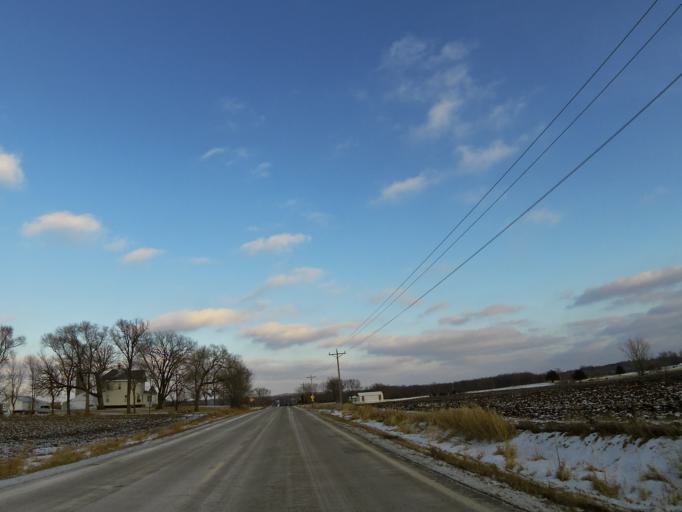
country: US
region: Minnesota
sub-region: Scott County
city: Prior Lake
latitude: 44.6524
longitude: -93.4754
